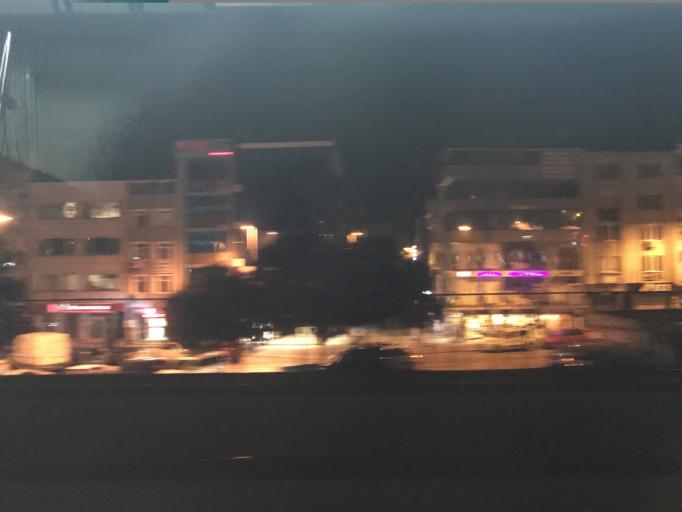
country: TR
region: Istanbul
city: Maltepe
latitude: 40.8897
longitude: 29.1884
